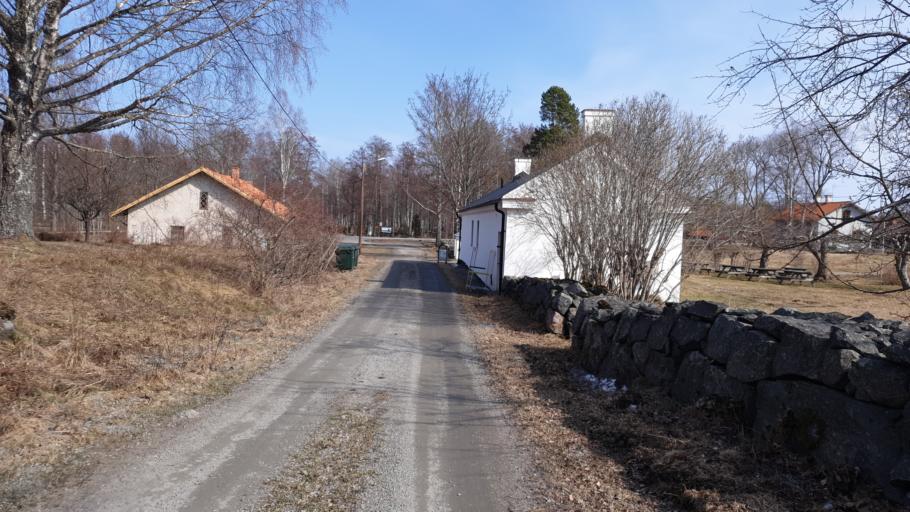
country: SE
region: Gaevleborg
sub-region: Gavle Kommun
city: Norrsundet
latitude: 61.0473
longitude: 17.1424
